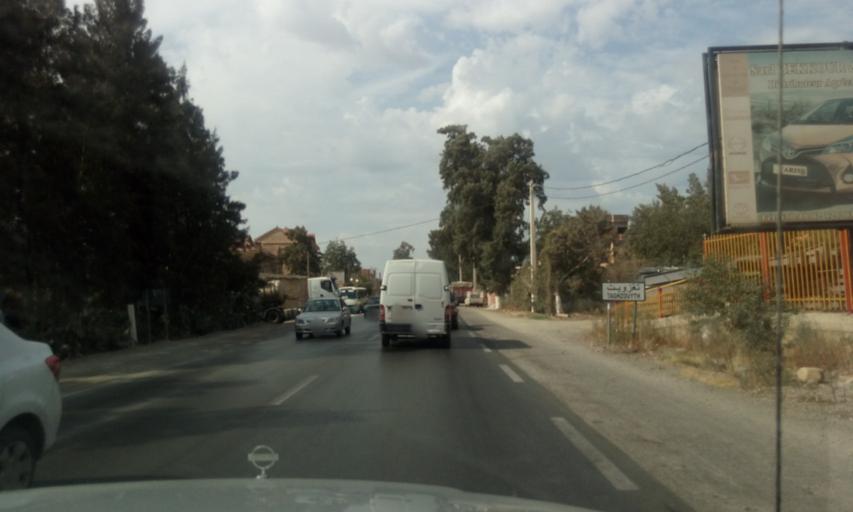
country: DZ
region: Bejaia
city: Seddouk
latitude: 36.5921
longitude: 4.6700
